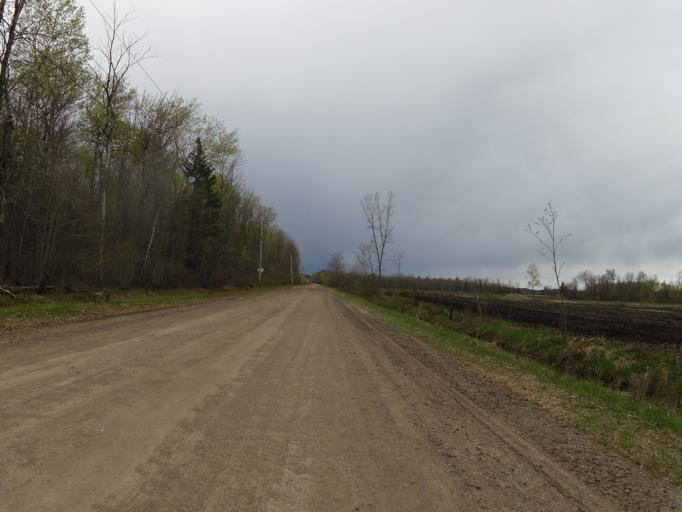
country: CA
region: Ontario
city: Hawkesbury
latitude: 45.6160
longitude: -74.5125
